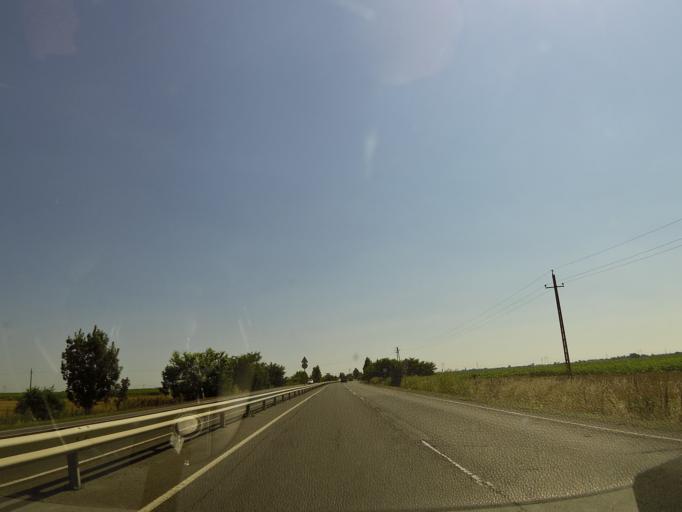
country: HU
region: Jasz-Nagykun-Szolnok
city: Szajol
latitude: 47.1783
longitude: 20.3280
